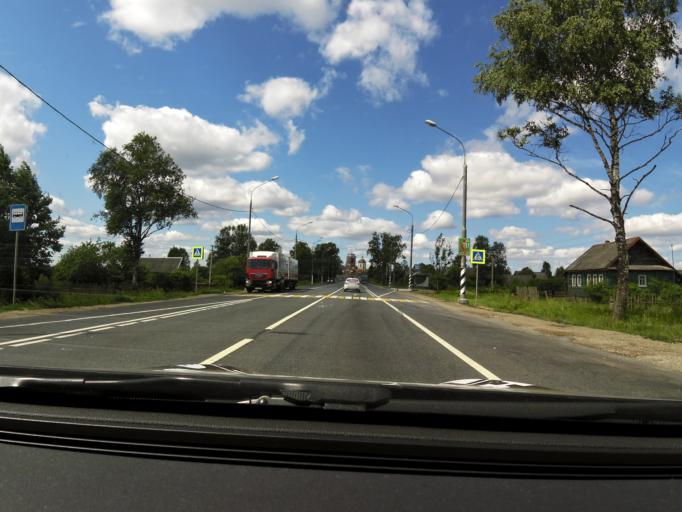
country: RU
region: Tverskaya
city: Kuzhenkino
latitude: 57.7222
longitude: 34.0923
